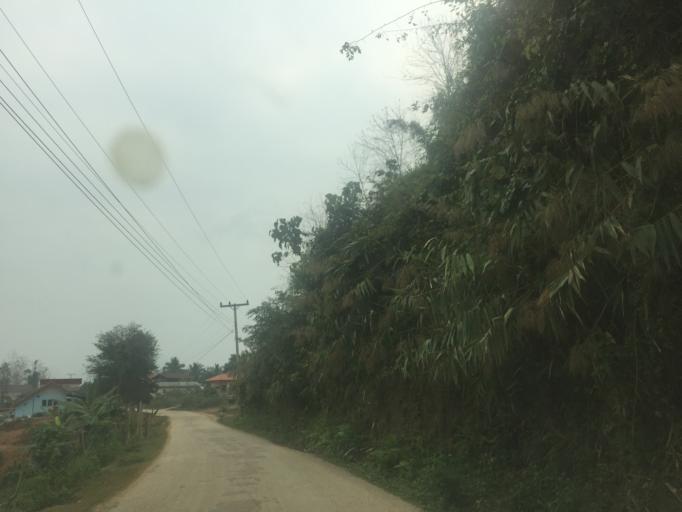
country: LA
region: Vientiane
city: Muang Sanakham
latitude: 18.3876
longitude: 101.5251
